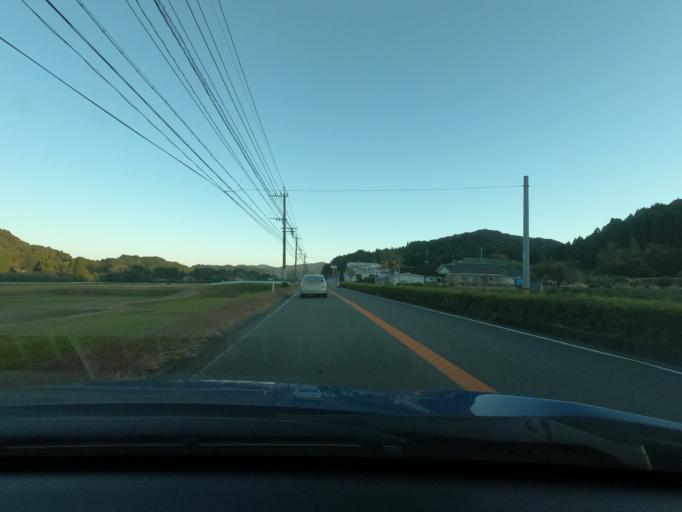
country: JP
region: Kagoshima
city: Satsumasendai
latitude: 31.8001
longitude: 130.4001
